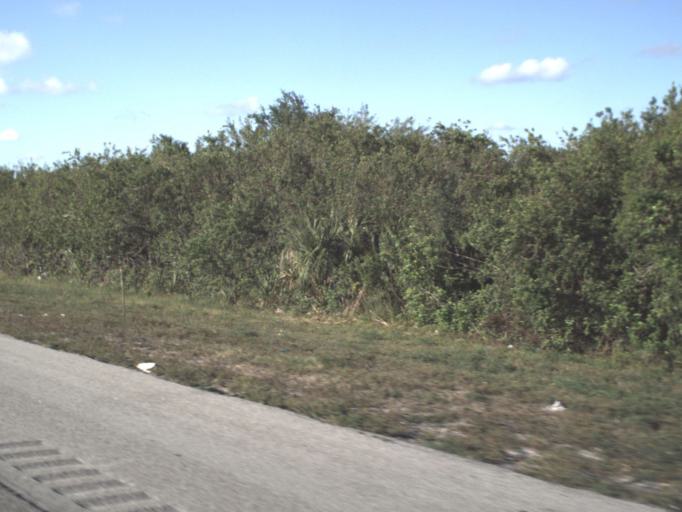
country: US
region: Florida
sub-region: Brevard County
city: Rockledge
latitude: 28.2694
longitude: -80.7297
